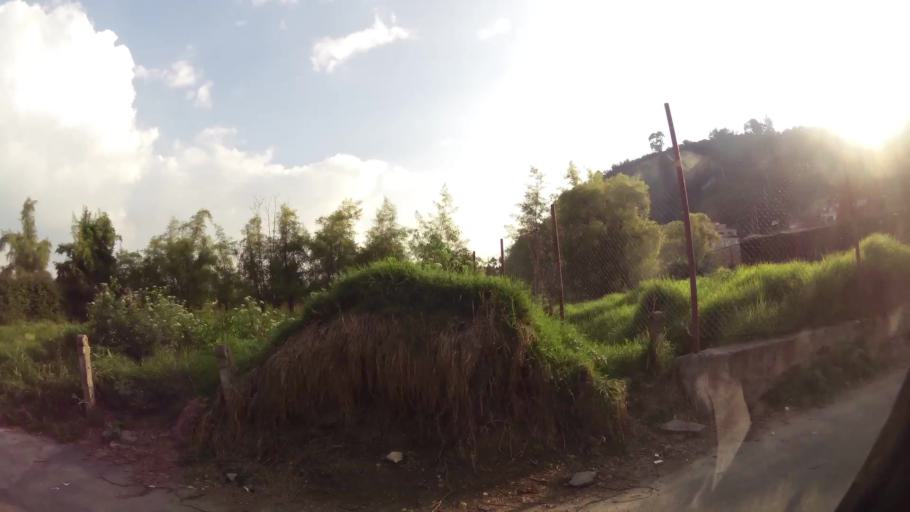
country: CO
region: Cundinamarca
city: Cota
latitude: 4.8139
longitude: -74.1061
